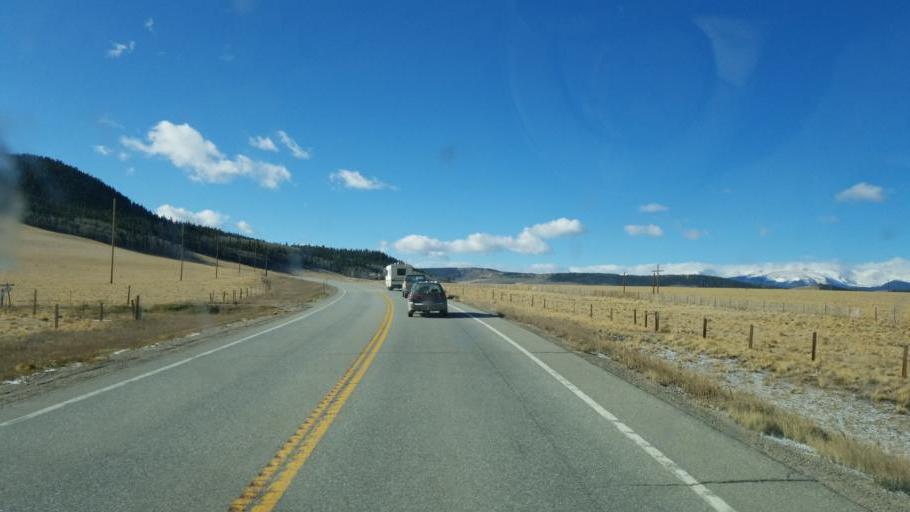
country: US
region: Colorado
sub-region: Park County
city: Fairplay
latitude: 39.2851
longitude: -105.9133
